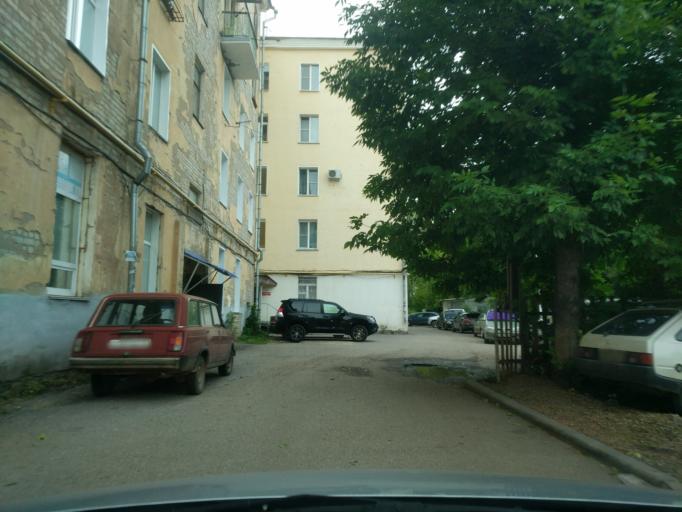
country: RU
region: Kirov
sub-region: Kirovo-Chepetskiy Rayon
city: Kirov
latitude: 58.6086
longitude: 49.6580
